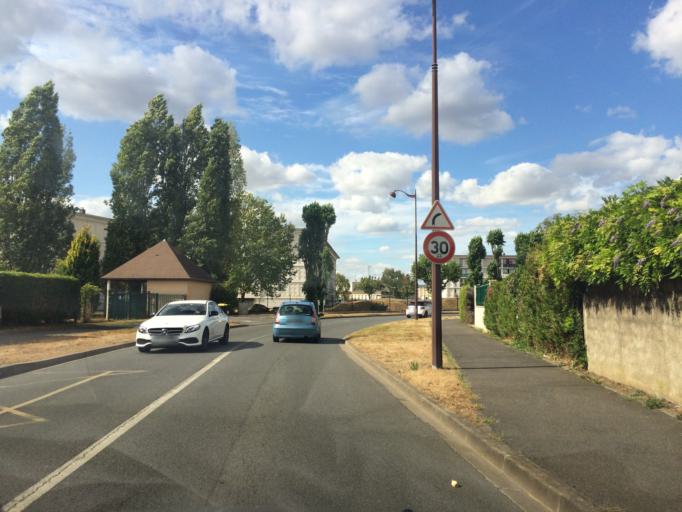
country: FR
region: Ile-de-France
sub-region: Departement de l'Essonne
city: Le Plessis-Pate
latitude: 48.6069
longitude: 2.3172
